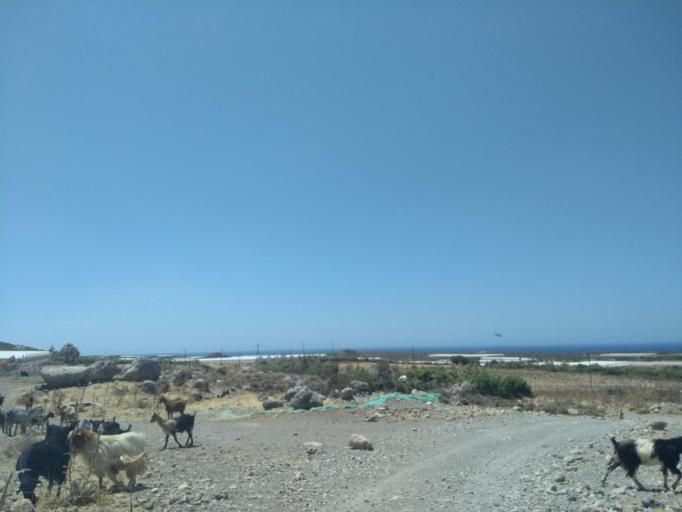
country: GR
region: Crete
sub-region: Nomos Chanias
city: Palaiochora
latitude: 35.3047
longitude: 23.5456
